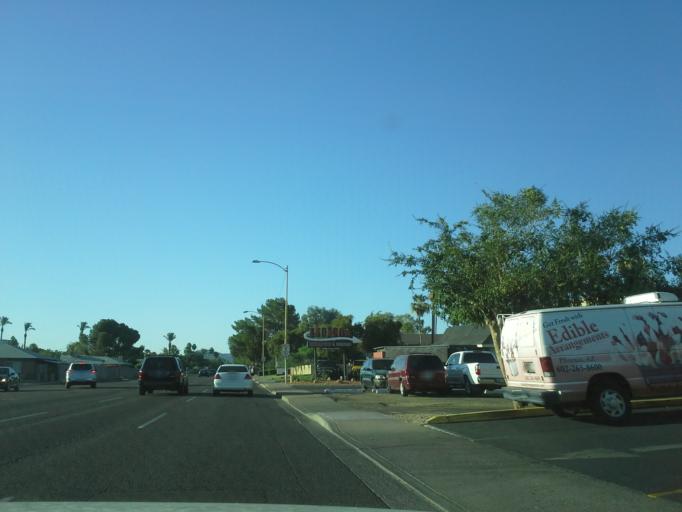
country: US
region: Arizona
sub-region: Maricopa County
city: Phoenix
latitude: 33.5170
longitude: -112.0824
